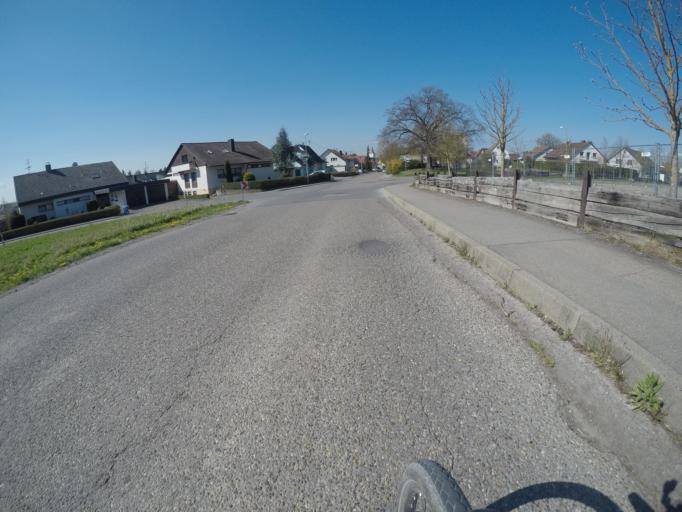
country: DE
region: Baden-Wuerttemberg
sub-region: Regierungsbezirk Stuttgart
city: Herrenberg
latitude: 48.5605
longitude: 8.9116
